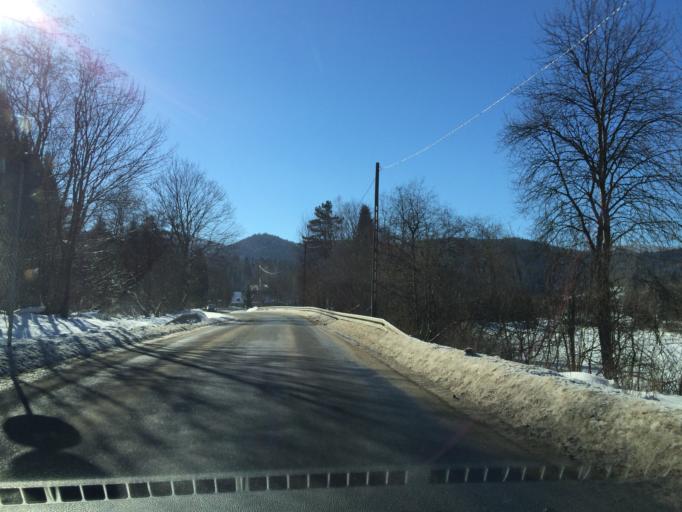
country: PL
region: Subcarpathian Voivodeship
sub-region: Powiat leski
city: Cisna
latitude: 49.2166
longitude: 22.3352
